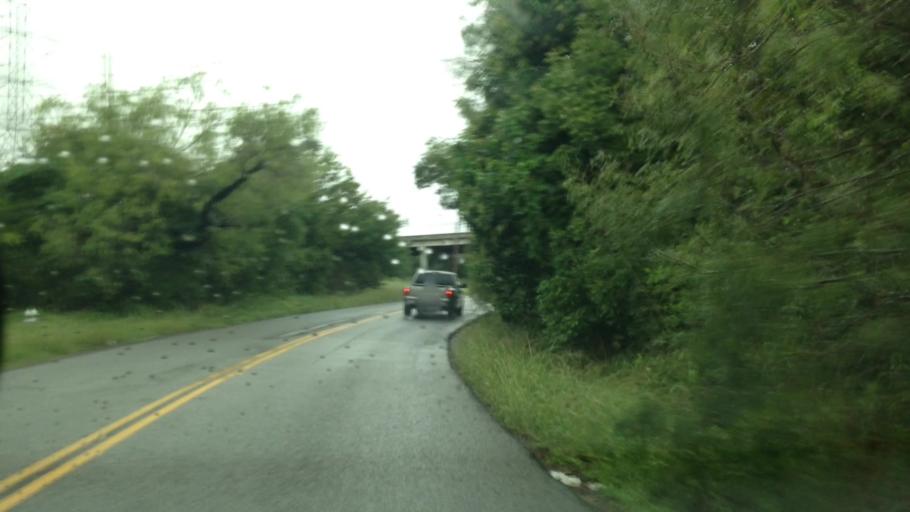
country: US
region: Texas
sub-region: Bexar County
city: Windcrest
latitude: 29.5523
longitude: -98.3822
